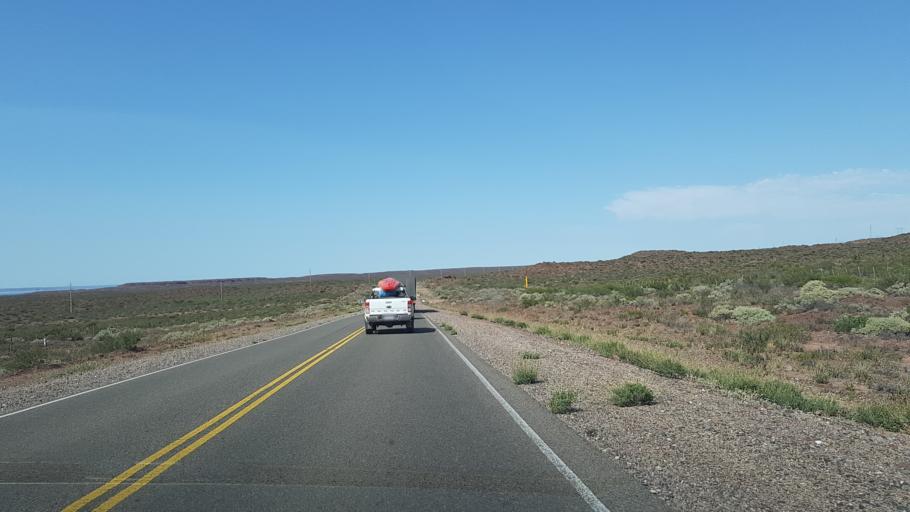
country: AR
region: Neuquen
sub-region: Departamento de Picun Leufu
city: Picun Leufu
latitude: -39.2797
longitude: -68.8595
